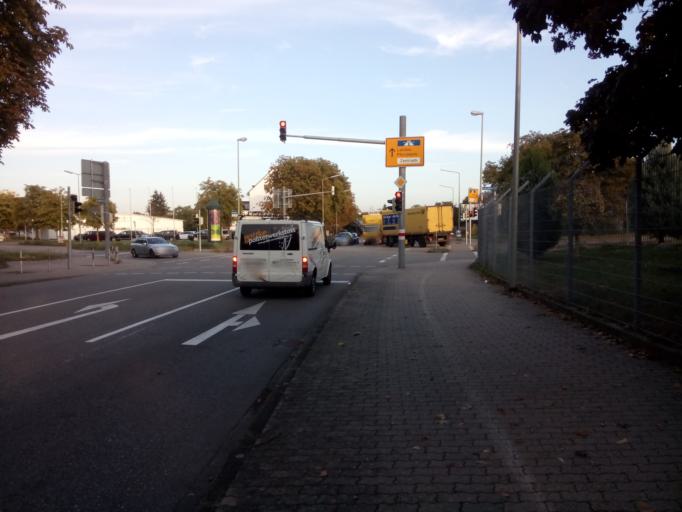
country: DE
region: Baden-Wuerttemberg
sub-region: Karlsruhe Region
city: Karlsruhe
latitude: 49.0026
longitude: 8.3591
